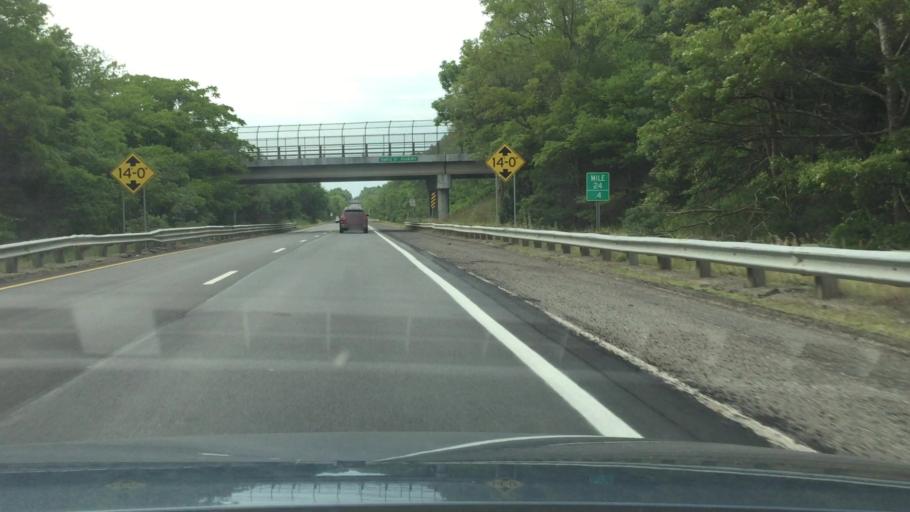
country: US
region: Massachusetts
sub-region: Plymouth County
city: Marshfield
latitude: 42.0803
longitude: -70.7387
